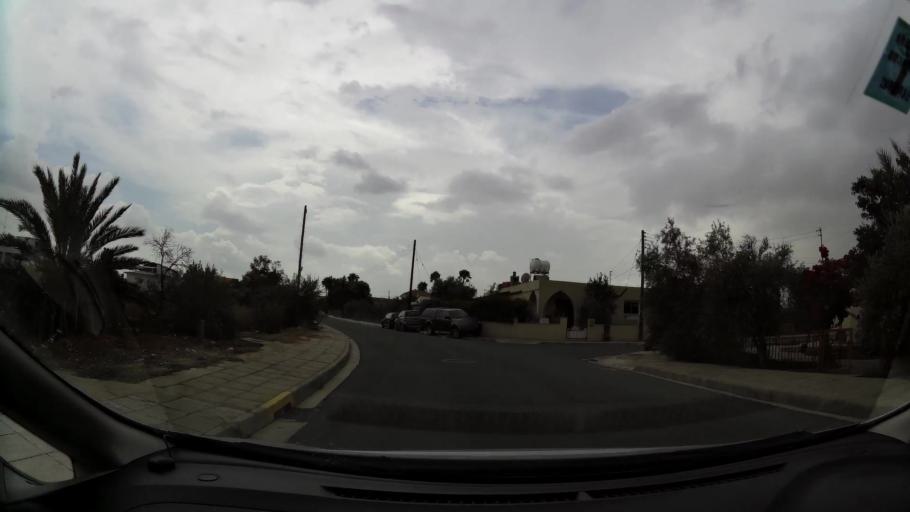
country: CY
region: Lefkosia
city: Geri
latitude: 35.1025
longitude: 33.3898
